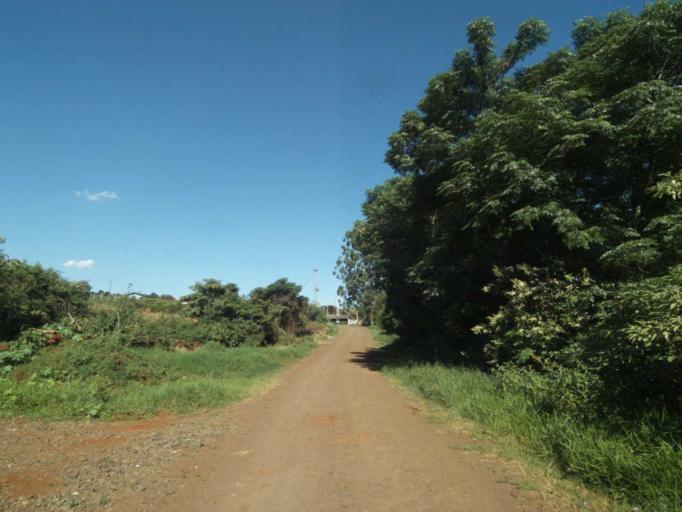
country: BR
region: Parana
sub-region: Laranjeiras Do Sul
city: Laranjeiras do Sul
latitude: -25.3847
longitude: -52.2008
